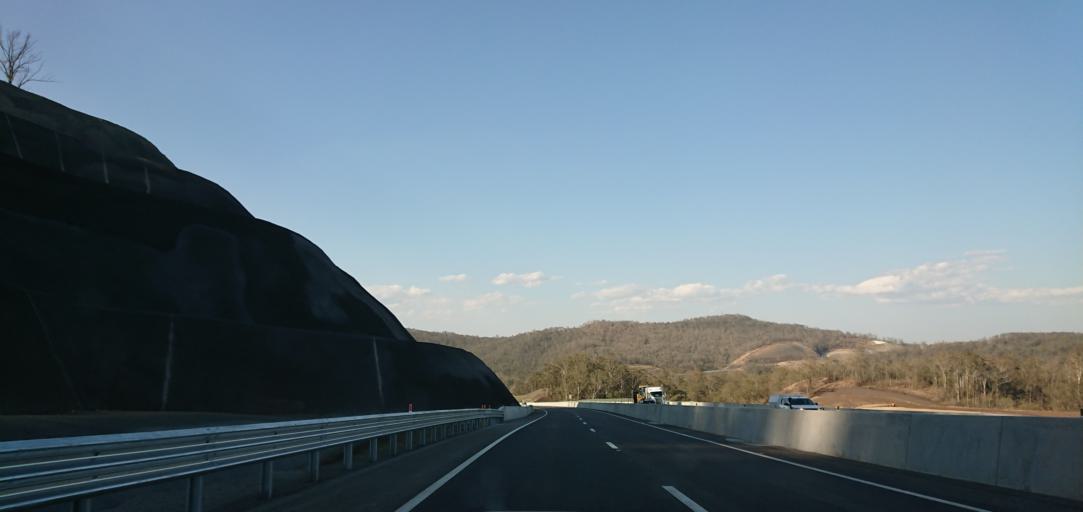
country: AU
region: Queensland
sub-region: Toowoomba
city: Wilsonton Heights
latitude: -27.5079
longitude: 151.9692
